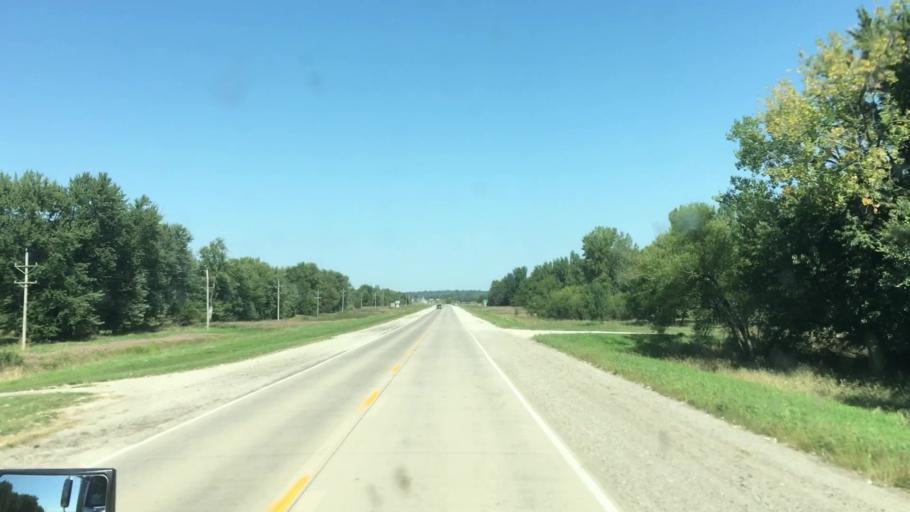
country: US
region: Iowa
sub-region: Benton County
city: Belle Plaine
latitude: 41.8612
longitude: -92.2779
